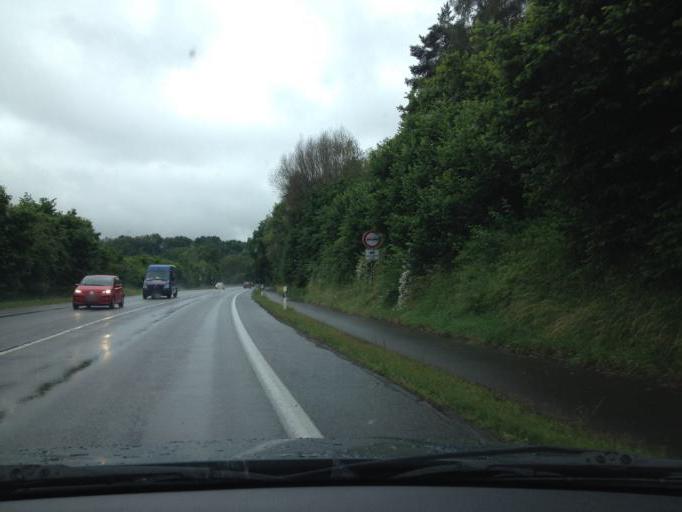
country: DE
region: Saarland
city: Ottweiler
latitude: 49.4174
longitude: 7.1599
